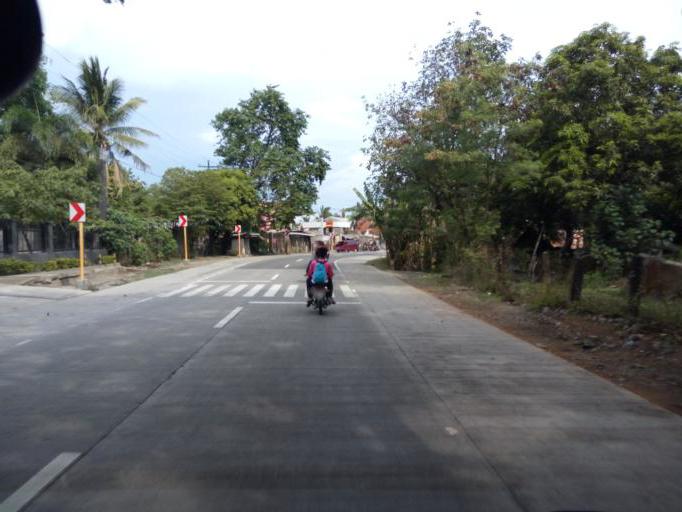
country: PH
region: Central Luzon
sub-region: Province of Nueva Ecija
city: Parista
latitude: 15.8327
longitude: 120.9450
